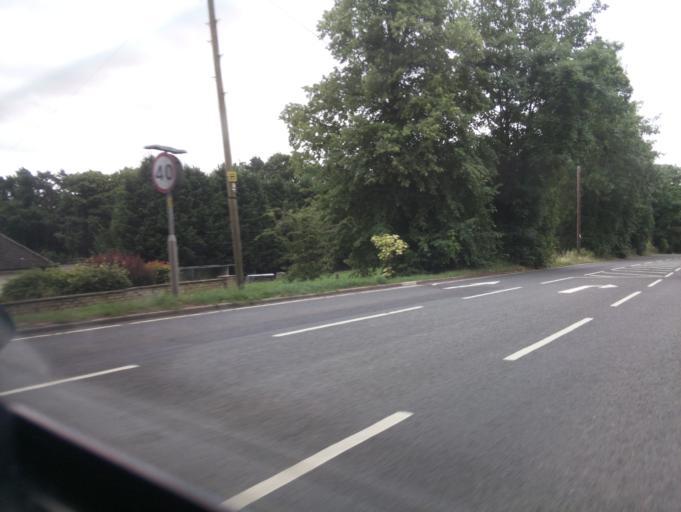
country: GB
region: England
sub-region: Worcestershire
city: Fernhill Heath
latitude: 52.2257
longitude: -2.2076
